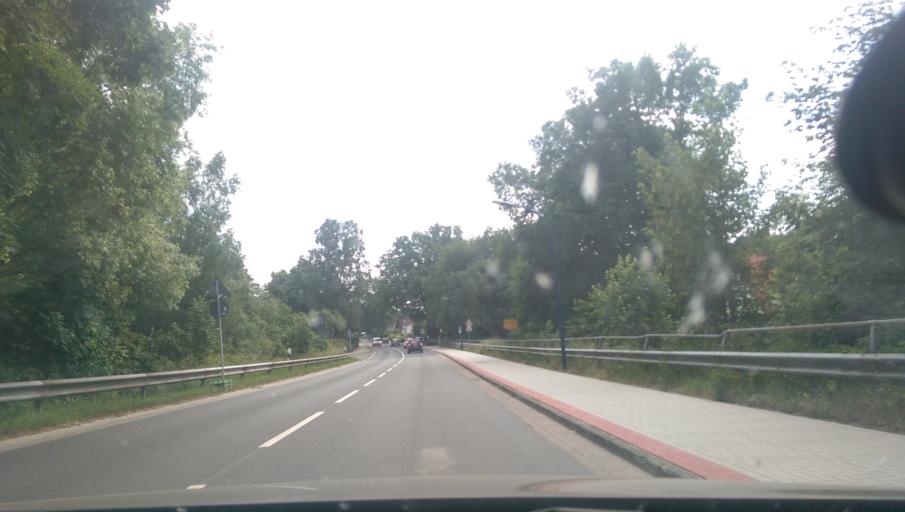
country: DE
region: Lower Saxony
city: Oyten
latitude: 53.0811
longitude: 9.0160
